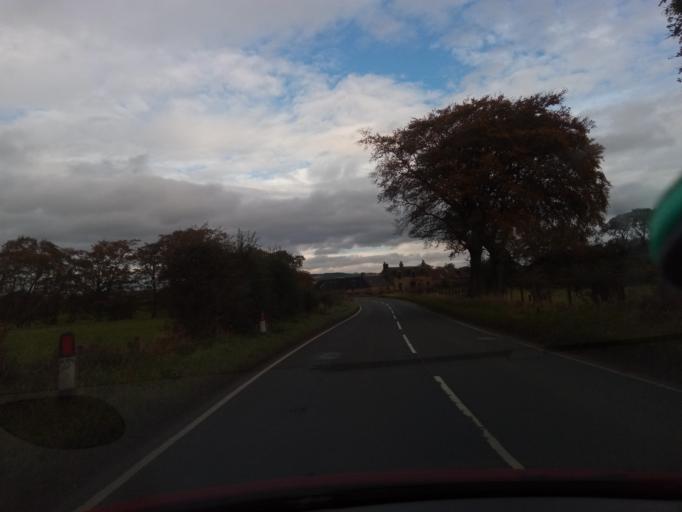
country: GB
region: Scotland
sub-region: West Lothian
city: Blackburn
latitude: 55.8644
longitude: -3.6237
